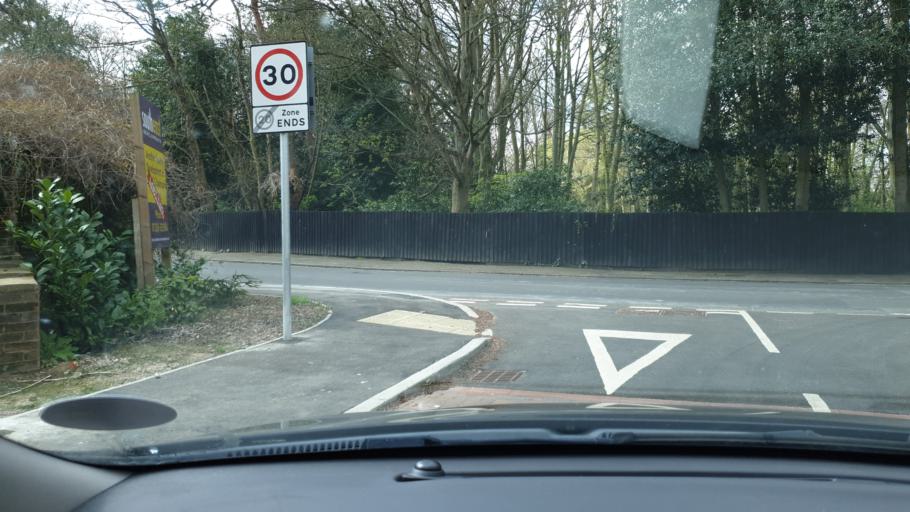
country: GB
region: England
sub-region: Suffolk
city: East Bergholt
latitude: 51.9212
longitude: 0.9866
